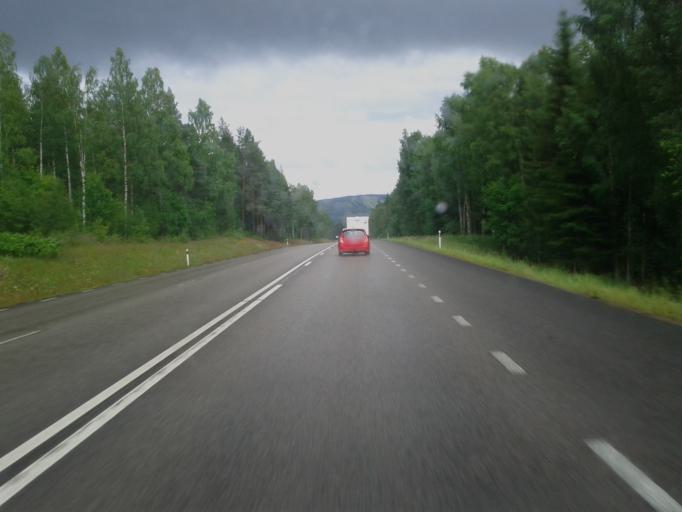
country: SE
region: Dalarna
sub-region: Rattviks Kommun
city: Raettvik
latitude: 60.9011
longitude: 15.0787
